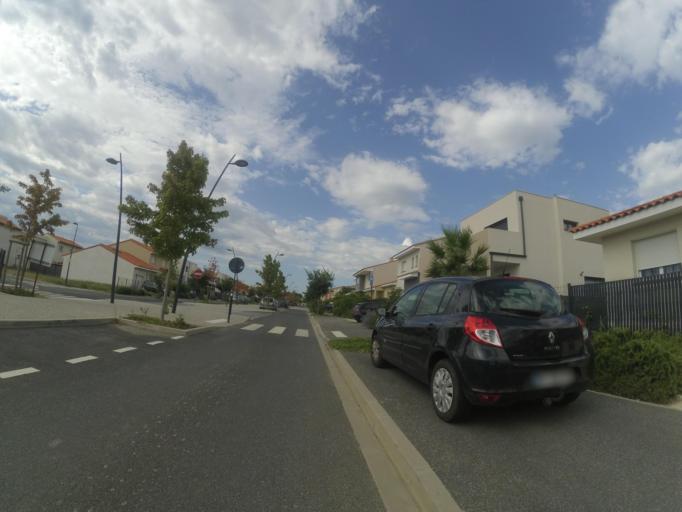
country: FR
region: Languedoc-Roussillon
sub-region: Departement des Pyrenees-Orientales
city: Toulouges
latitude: 42.6754
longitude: 2.8280
